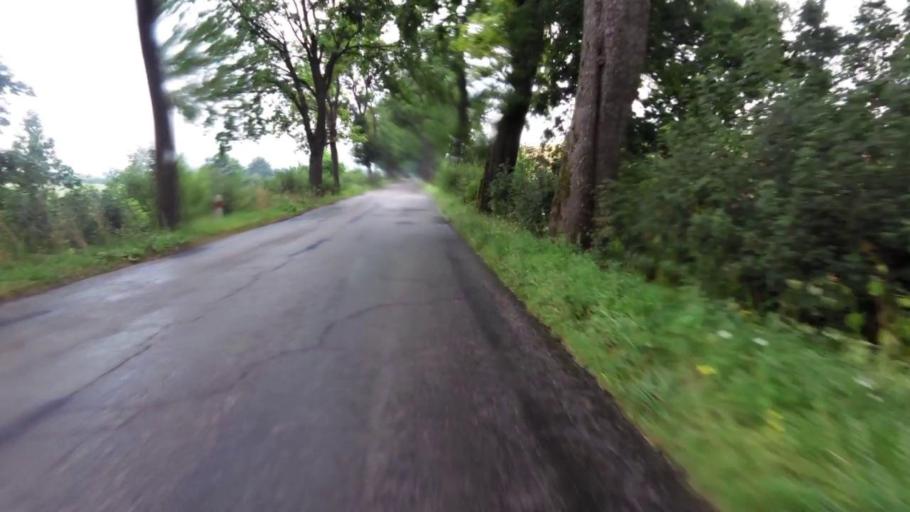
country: PL
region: West Pomeranian Voivodeship
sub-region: Powiat drawski
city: Czaplinek
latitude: 53.6005
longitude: 16.2527
